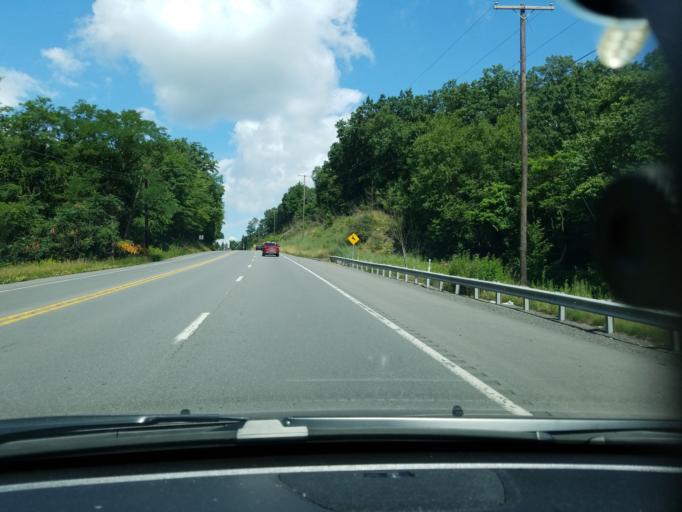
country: US
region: Pennsylvania
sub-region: Northumberland County
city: Kulpmont
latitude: 40.8135
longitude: -76.4535
